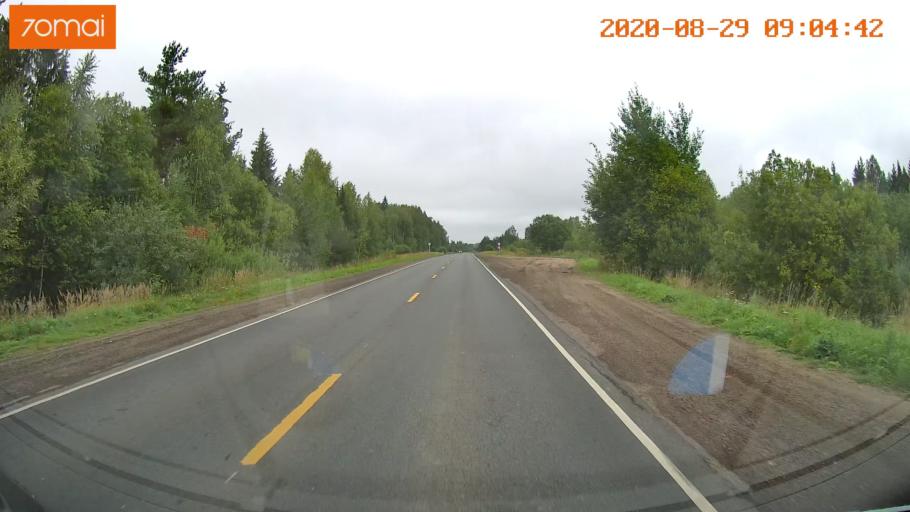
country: RU
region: Ivanovo
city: Navoloki
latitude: 57.3508
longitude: 41.9876
